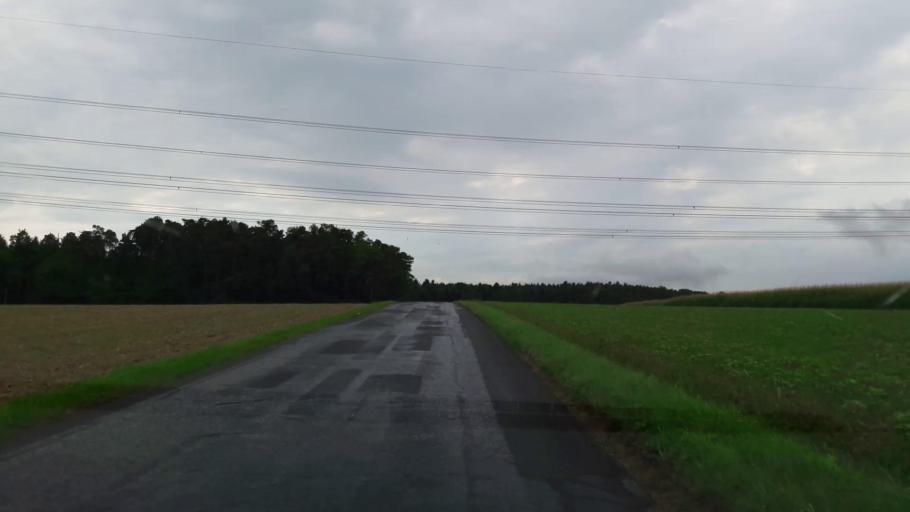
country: AT
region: Styria
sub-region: Politischer Bezirk Hartberg-Fuerstenfeld
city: Sankt Johann in der Haide
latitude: 47.2731
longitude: 16.0219
